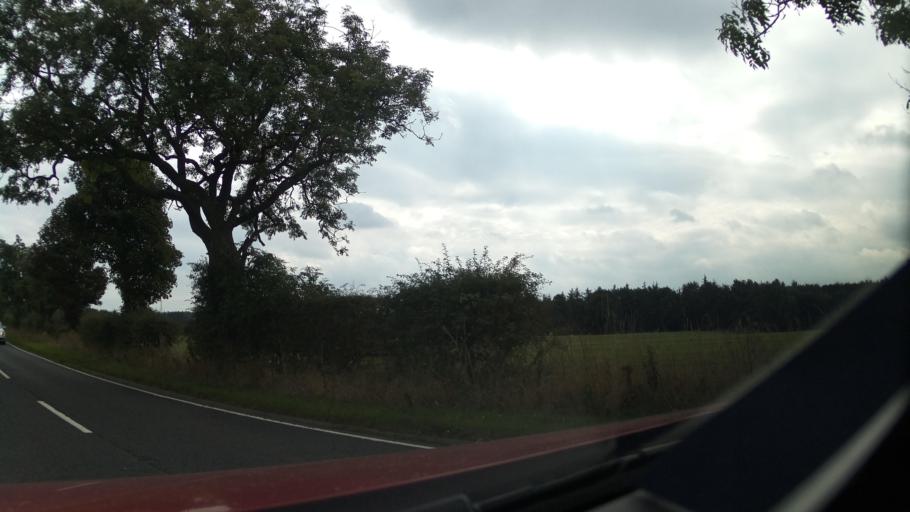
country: GB
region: England
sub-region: Northumberland
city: Darras Hall
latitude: 55.0674
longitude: -1.7859
